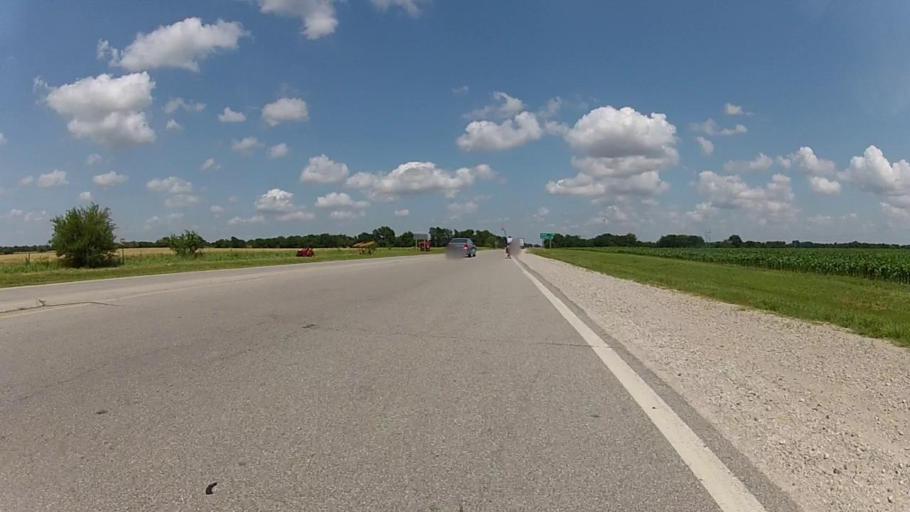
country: US
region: Kansas
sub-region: Labette County
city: Altamont
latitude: 37.1935
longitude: -95.2664
